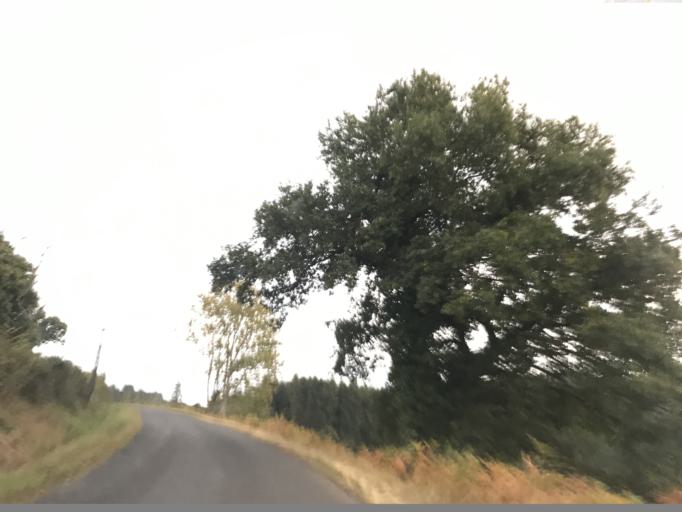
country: FR
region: Auvergne
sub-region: Departement du Puy-de-Dome
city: Celles-sur-Durolle
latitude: 45.8403
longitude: 3.6280
